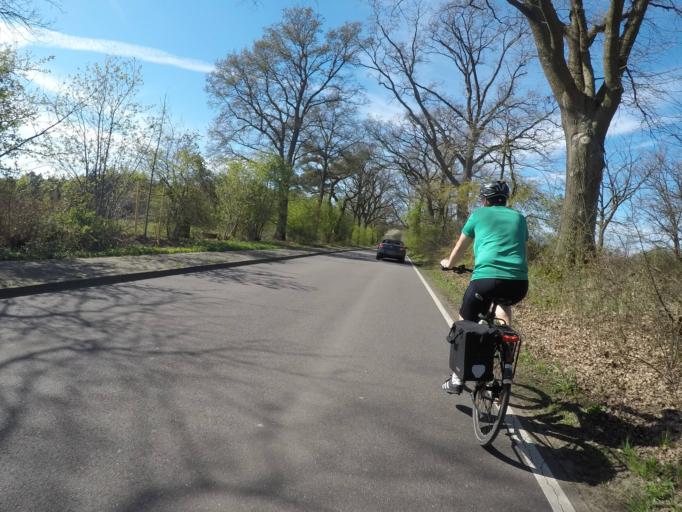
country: DE
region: Schleswig-Holstein
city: Tangstedt
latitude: 53.7129
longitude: 10.0809
